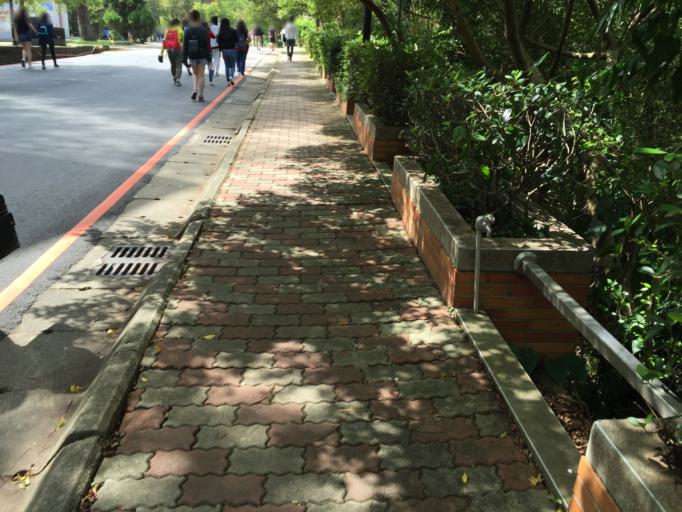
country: TW
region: Taiwan
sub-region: Hsinchu
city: Hsinchu
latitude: 24.7593
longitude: 120.9545
